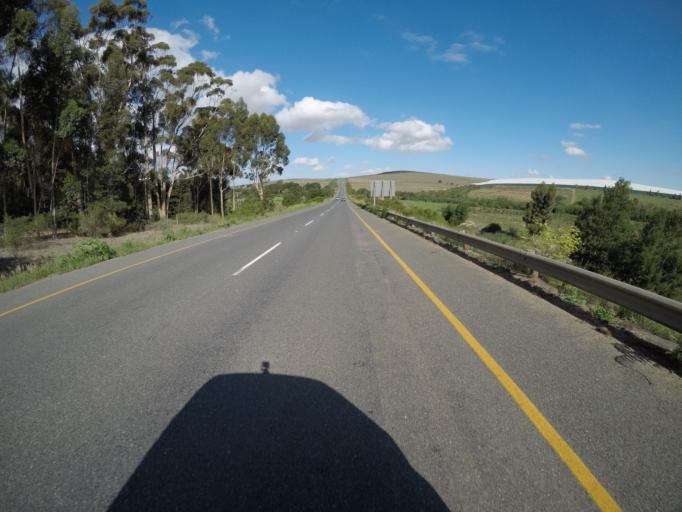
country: ZA
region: Western Cape
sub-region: Overberg District Municipality
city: Swellendam
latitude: -33.9624
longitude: 20.2426
